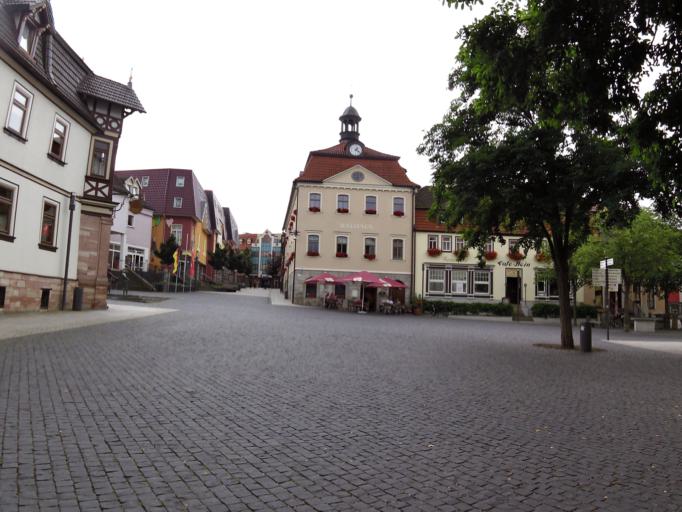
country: DE
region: Thuringia
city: Bad Salzungen
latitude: 50.8130
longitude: 10.2359
